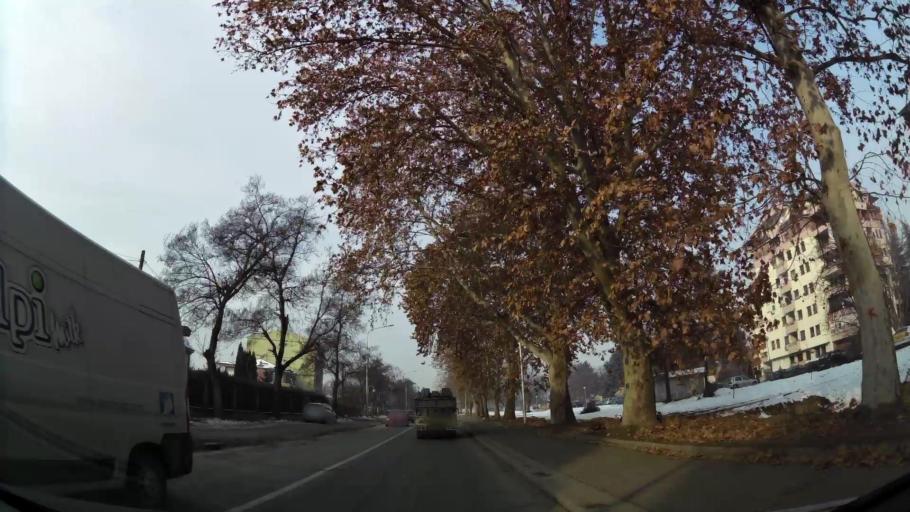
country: MK
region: Butel
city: Butel
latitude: 42.0245
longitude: 21.4490
